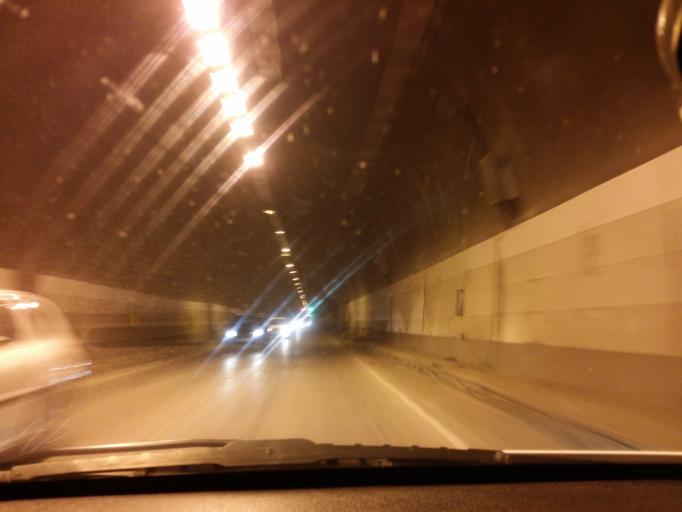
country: IR
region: Tehran
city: Tajrish
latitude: 36.1601
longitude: 51.3148
